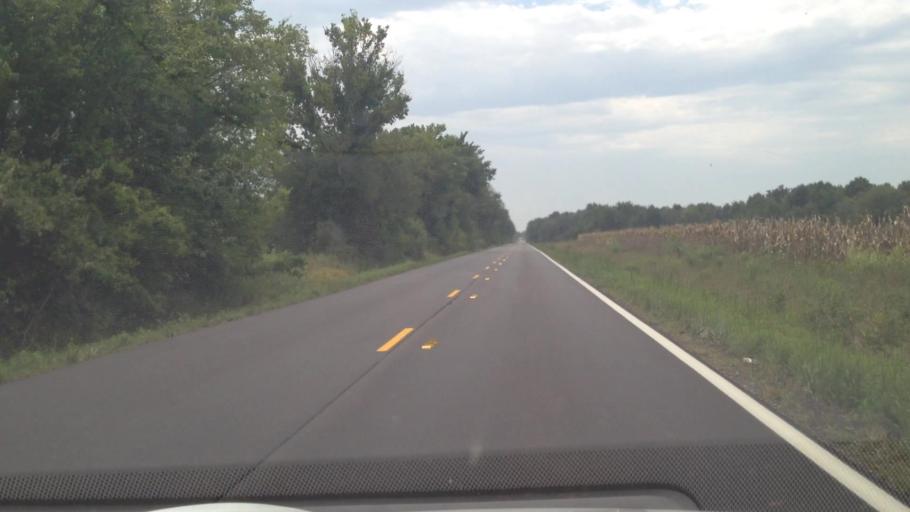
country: US
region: Kansas
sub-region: Crawford County
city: Girard
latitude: 37.5277
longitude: -94.9606
